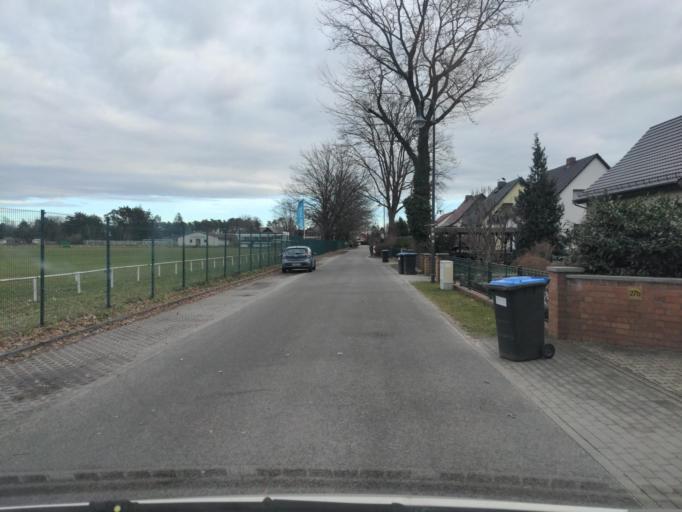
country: DE
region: Brandenburg
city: Cottbus
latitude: 51.7132
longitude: 14.3298
